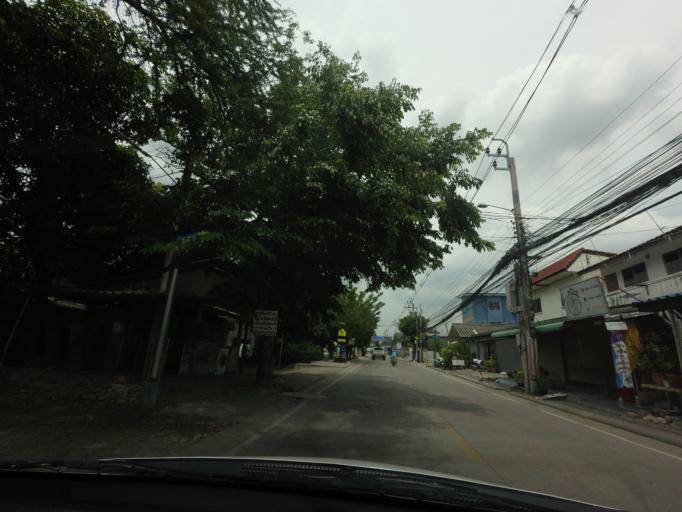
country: TH
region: Nonthaburi
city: Mueang Nonthaburi
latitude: 13.8892
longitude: 100.5191
